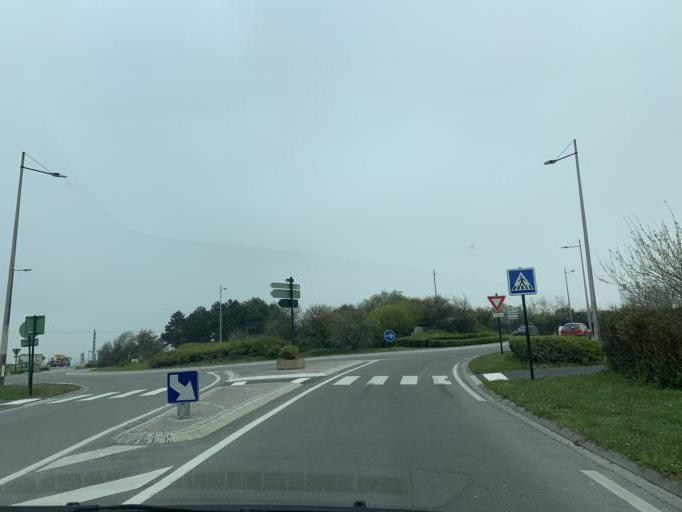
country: FR
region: Nord-Pas-de-Calais
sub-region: Departement du Pas-de-Calais
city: Marquise
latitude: 50.8237
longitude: 1.7070
